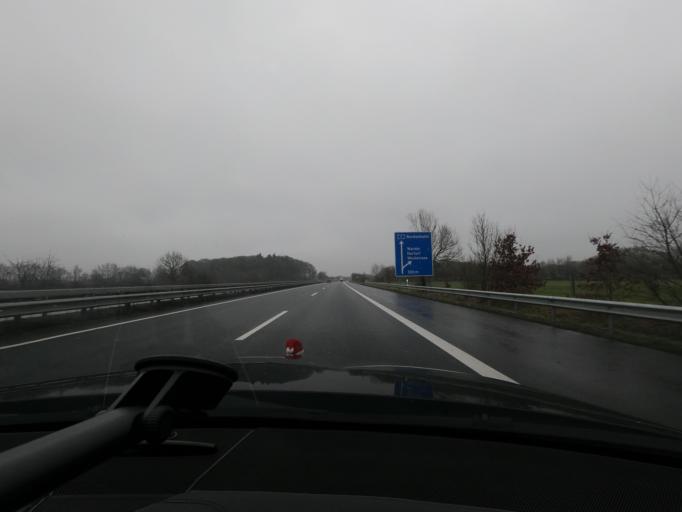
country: DE
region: Schleswig-Holstein
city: Gross Vollstedt
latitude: 54.2213
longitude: 9.8513
